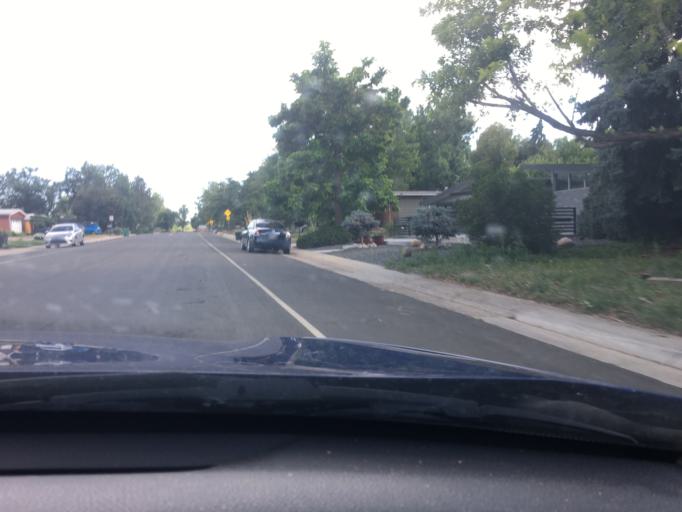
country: US
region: Colorado
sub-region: Jefferson County
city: Applewood
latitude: 39.7666
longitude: -105.1380
